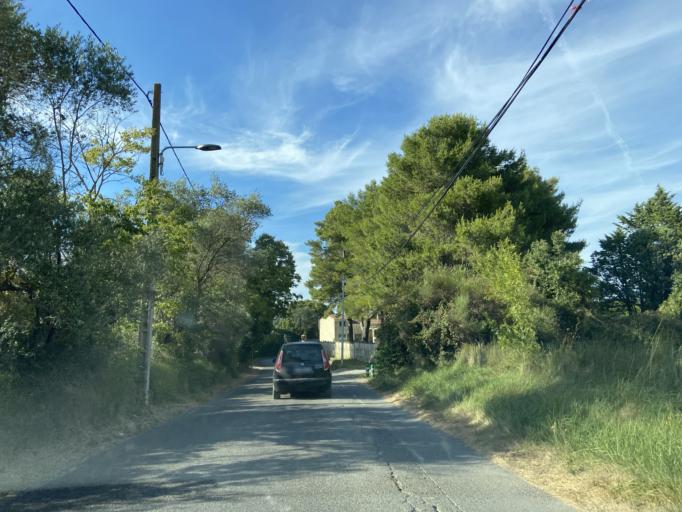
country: FR
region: Provence-Alpes-Cote d'Azur
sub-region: Departement des Bouches-du-Rhone
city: Miramas
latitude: 43.5689
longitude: 5.0193
